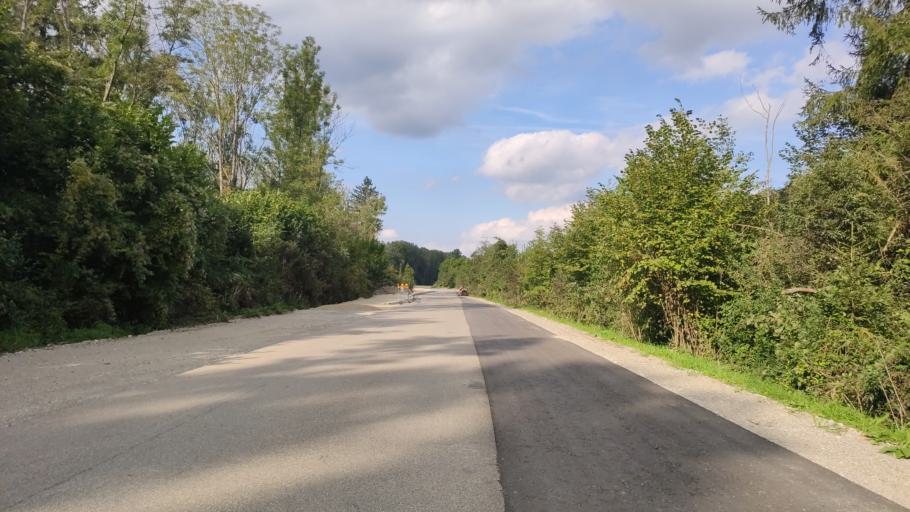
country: DE
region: Bavaria
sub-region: Upper Bavaria
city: Scheuring
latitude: 48.1565
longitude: 10.8784
